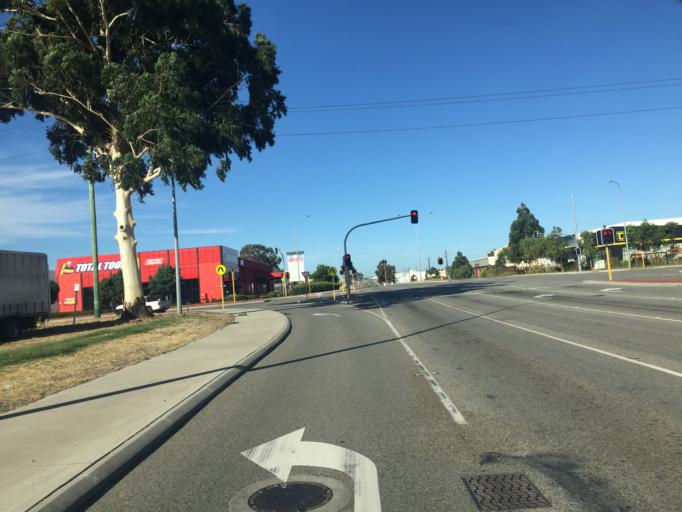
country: AU
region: Western Australia
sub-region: Belmont
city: Kewdale
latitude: -31.9801
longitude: 115.9591
